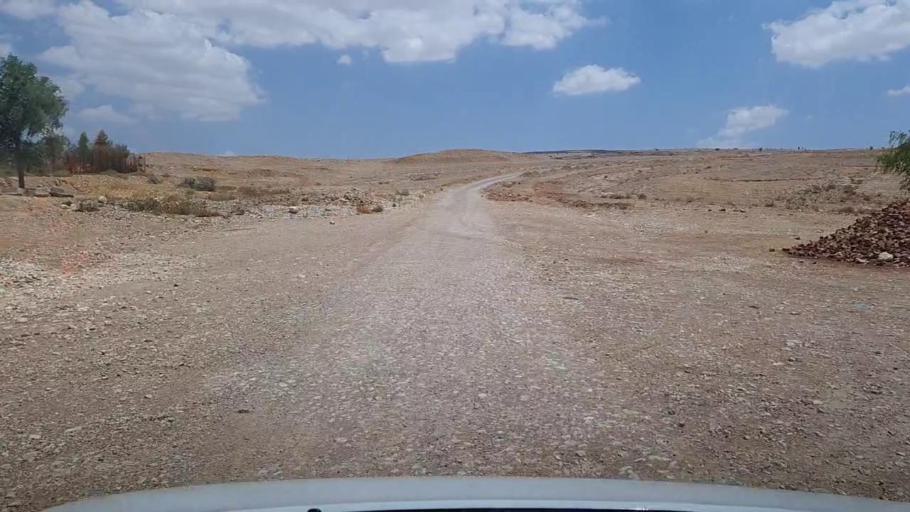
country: PK
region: Sindh
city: Bhan
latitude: 26.2919
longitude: 67.5801
